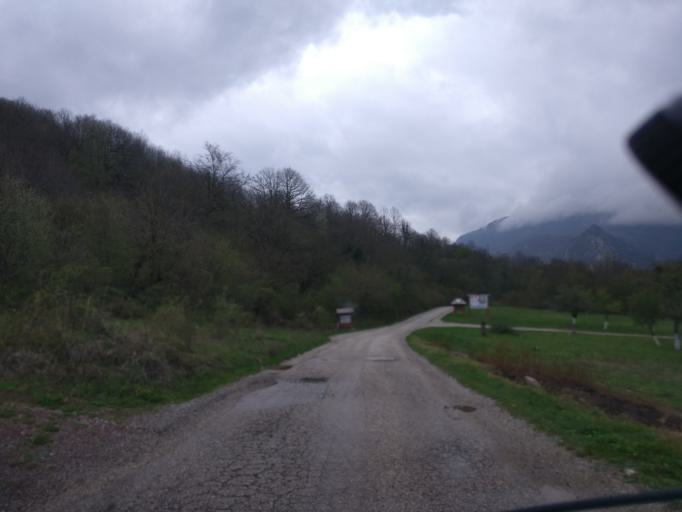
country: BA
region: Republika Srpska
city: Foca
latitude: 43.3532
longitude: 18.8249
